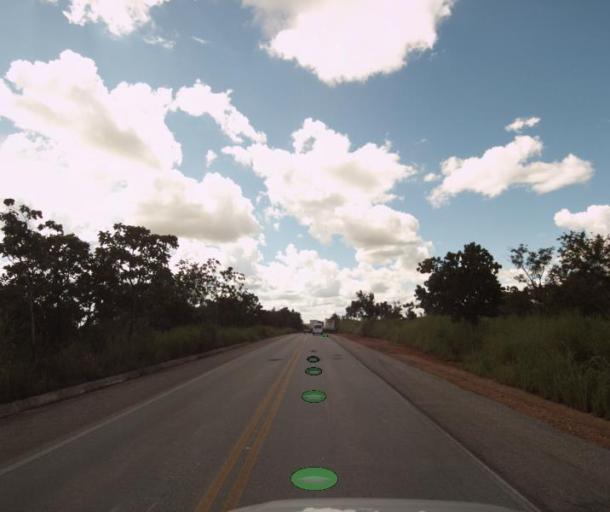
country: BR
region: Goias
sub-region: Porangatu
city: Porangatu
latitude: -13.6391
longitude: -49.0408
